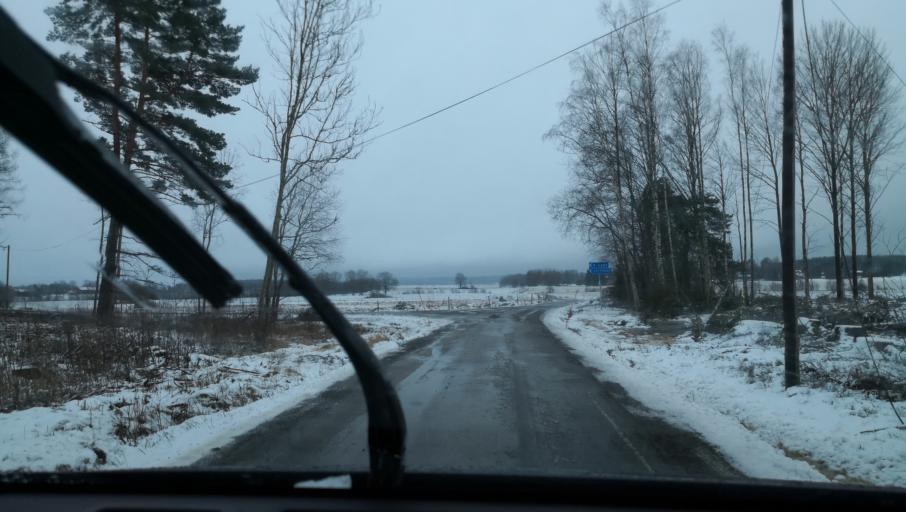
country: SE
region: Vaestmanland
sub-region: Kopings Kommun
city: Kolsva
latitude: 59.5429
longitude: 15.8817
